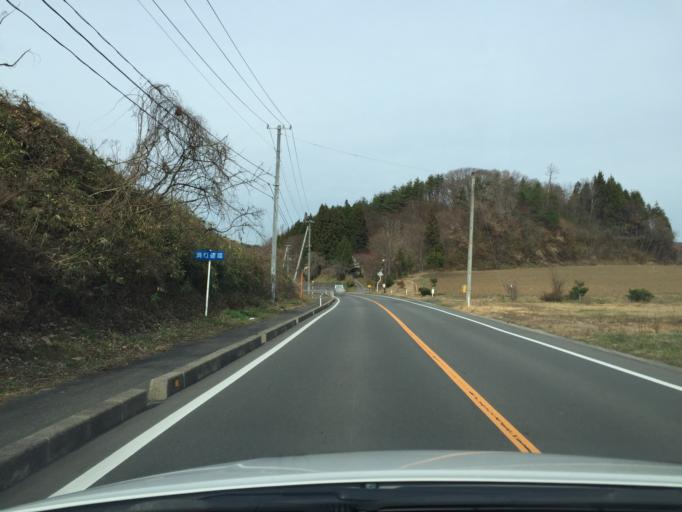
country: JP
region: Fukushima
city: Funehikimachi-funehiki
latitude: 37.3517
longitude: 140.6065
